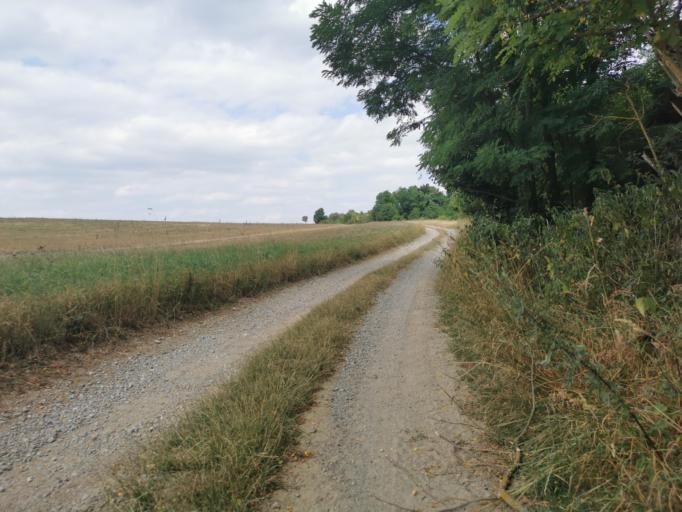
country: SK
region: Nitriansky
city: Brezova pod Bradlom
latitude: 48.6776
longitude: 17.4985
